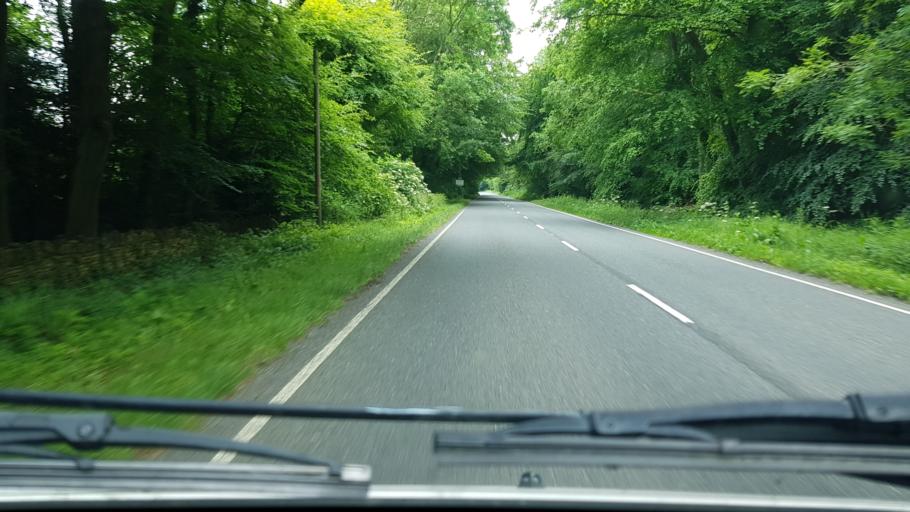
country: GB
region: England
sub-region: Gloucestershire
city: Donnington
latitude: 51.9796
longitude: -1.7647
